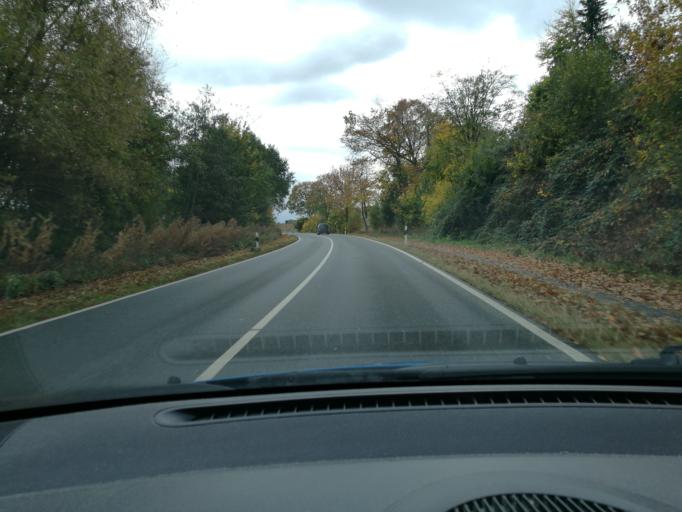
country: DE
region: Schleswig-Holstein
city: Pogeez
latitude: 53.7456
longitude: 10.7292
